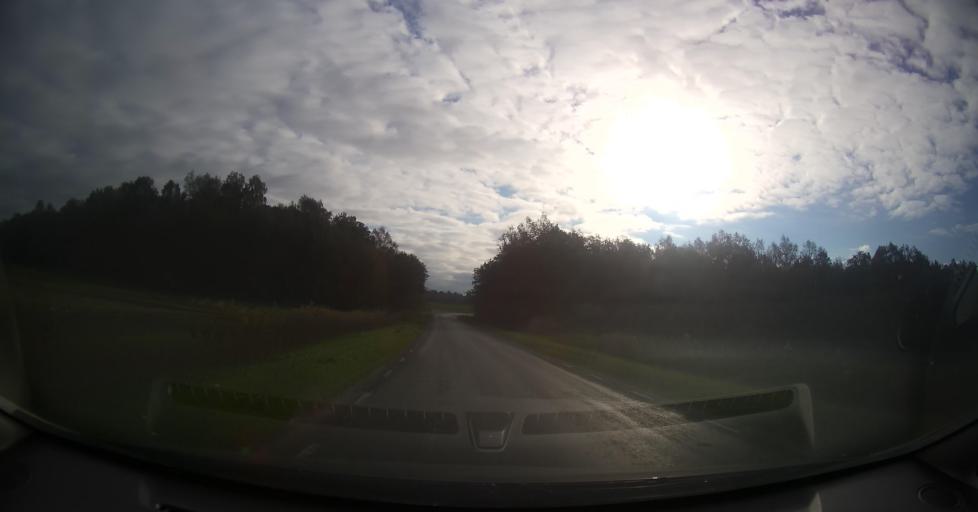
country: EE
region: Harju
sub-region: Raasiku vald
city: Raasiku
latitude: 59.3867
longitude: 25.1653
